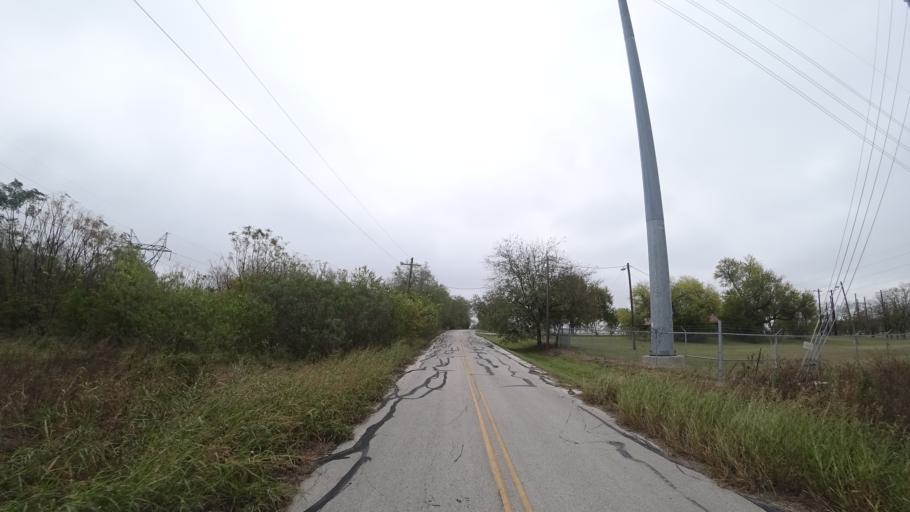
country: US
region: Texas
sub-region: Travis County
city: Pflugerville
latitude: 30.3832
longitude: -97.6404
